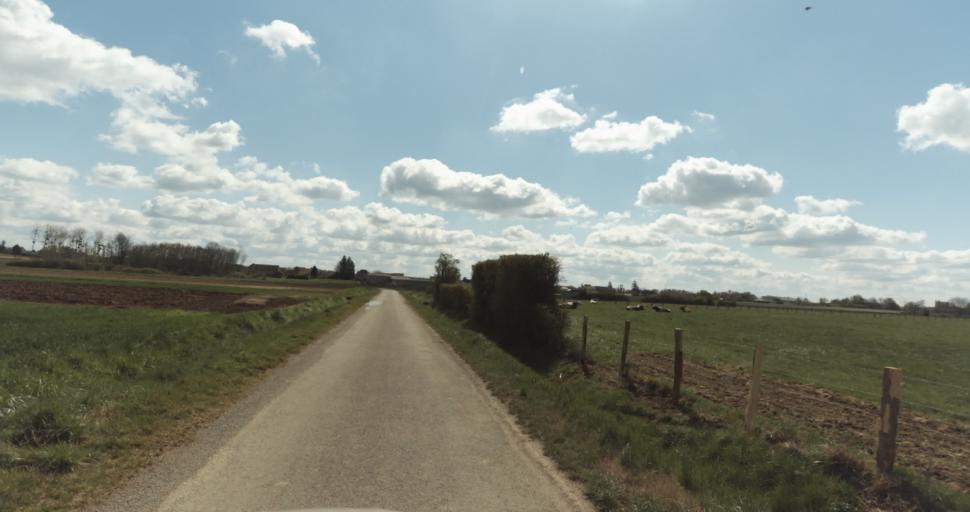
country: FR
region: Bourgogne
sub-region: Departement de la Cote-d'Or
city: Auxonne
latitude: 47.2122
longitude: 5.4067
